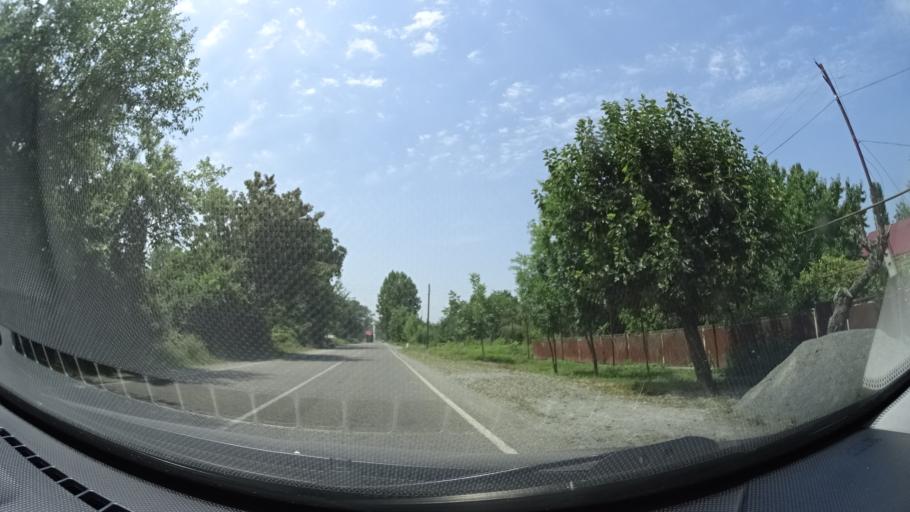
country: GE
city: Bagdadi
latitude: 41.7618
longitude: 46.1193
